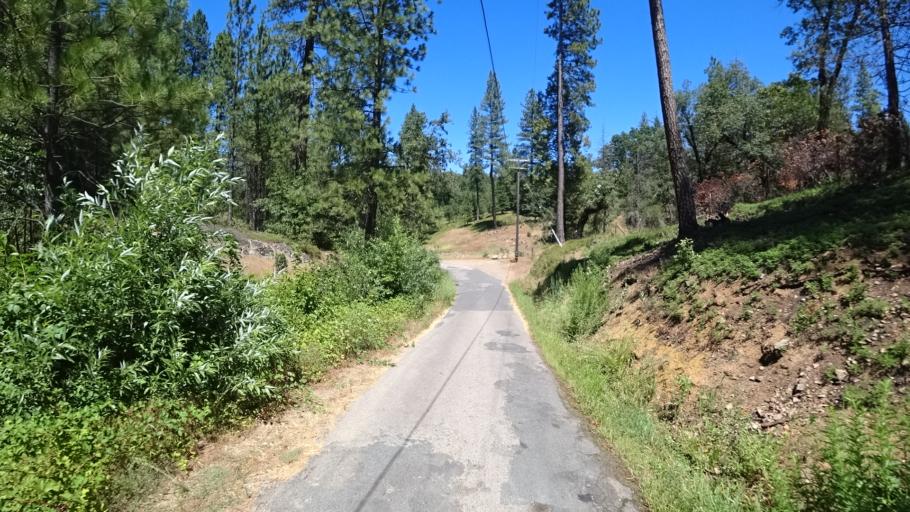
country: US
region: California
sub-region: Calaveras County
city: Mountain Ranch
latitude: 38.2746
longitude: -120.4624
